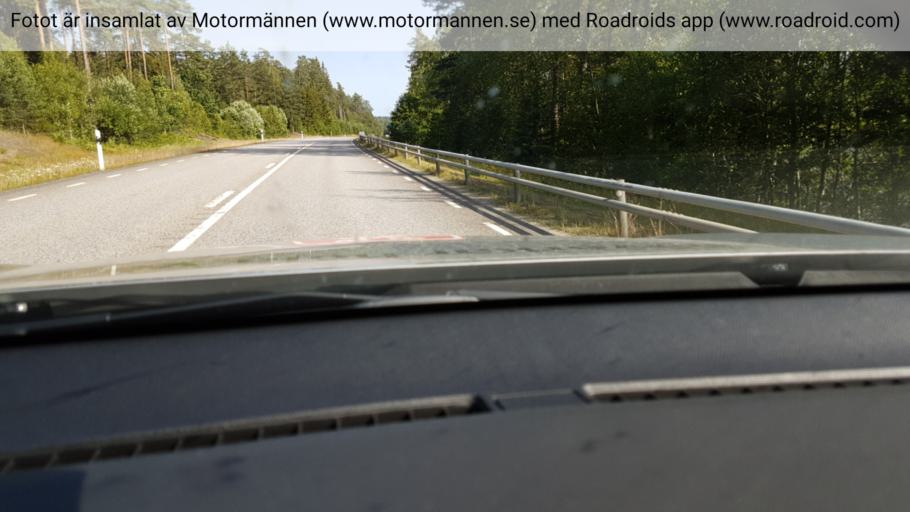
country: SE
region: Joenkoeping
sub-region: Aneby Kommun
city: Aneby
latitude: 57.7675
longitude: 14.9020
